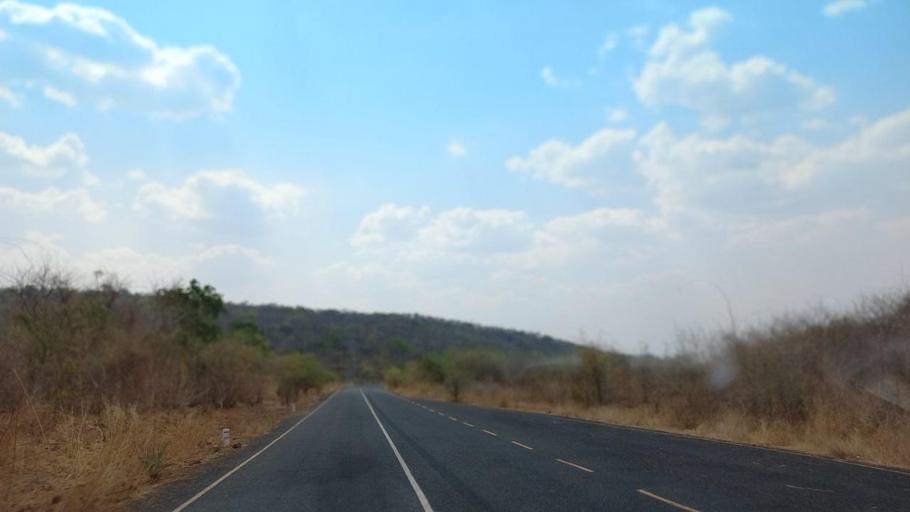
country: ZM
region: Lusaka
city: Luangwa
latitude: -15.3265
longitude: 30.3445
